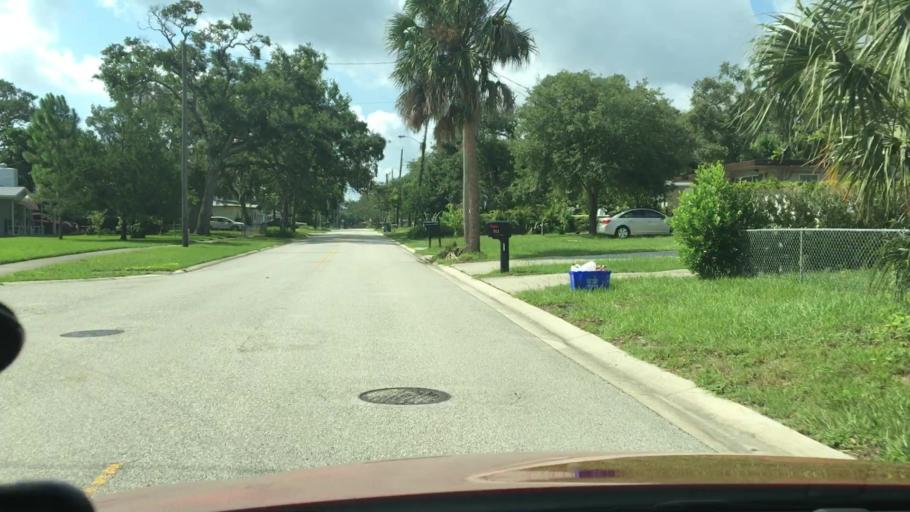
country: US
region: Florida
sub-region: Volusia County
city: Ormond Beach
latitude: 29.2716
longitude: -81.0523
